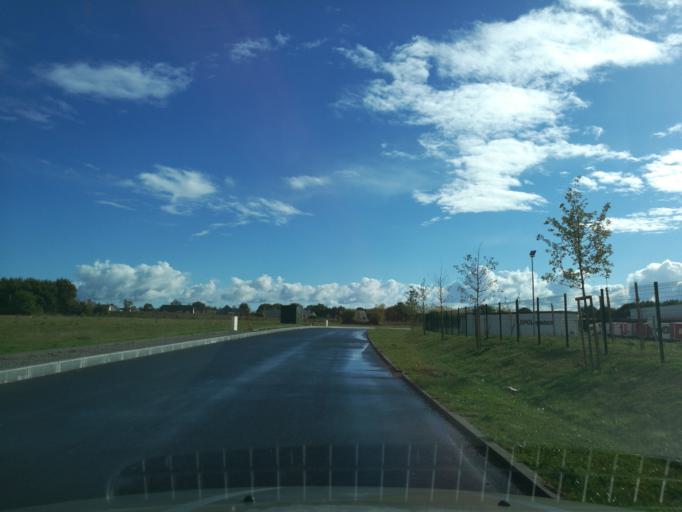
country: FR
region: Brittany
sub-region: Departement d'Ille-et-Vilaine
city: Pleumeleuc
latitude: 48.1865
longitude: -1.9326
